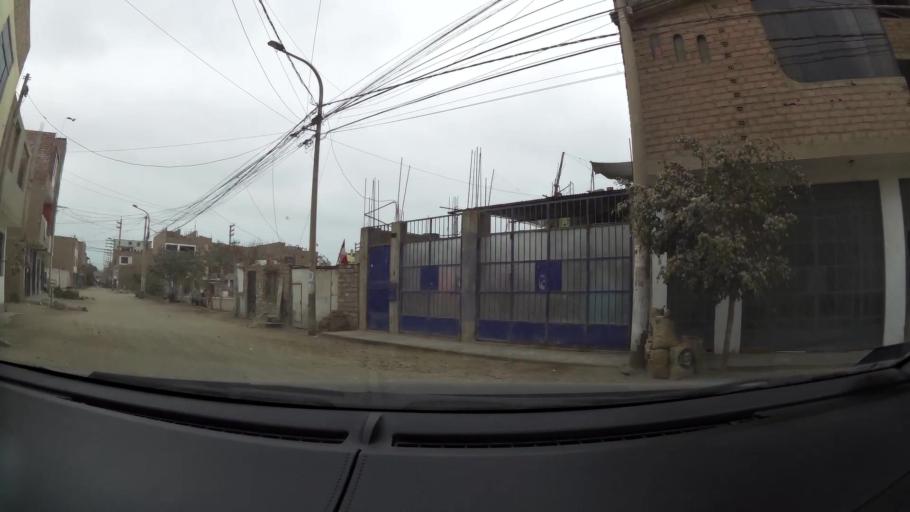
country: PE
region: Lima
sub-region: Lima
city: Independencia
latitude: -11.9628
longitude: -77.0945
